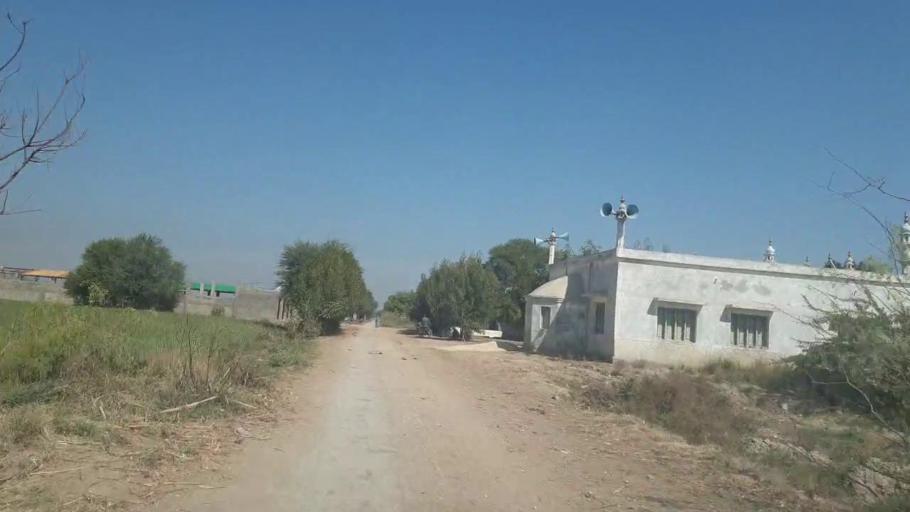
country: PK
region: Sindh
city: Mirpur Khas
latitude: 25.5447
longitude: 69.1965
